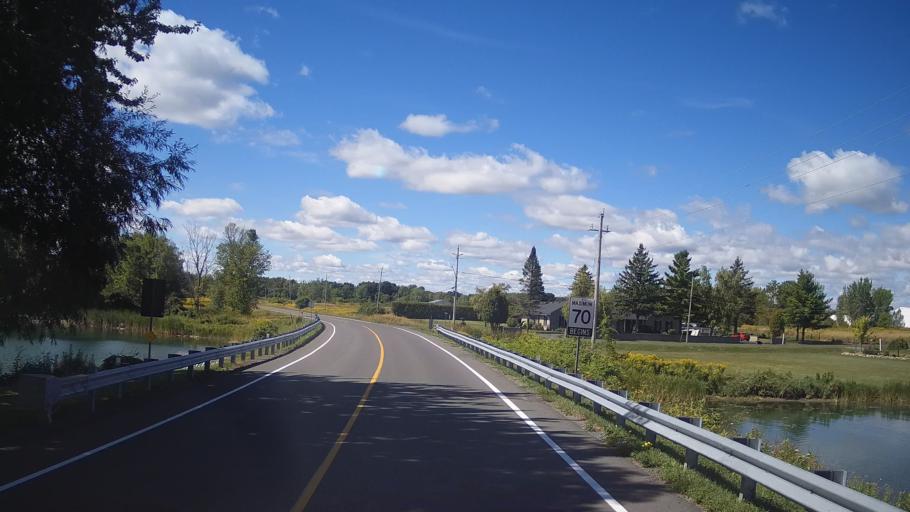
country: US
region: New York
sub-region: St. Lawrence County
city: Norfolk
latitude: 44.8738
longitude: -75.2389
